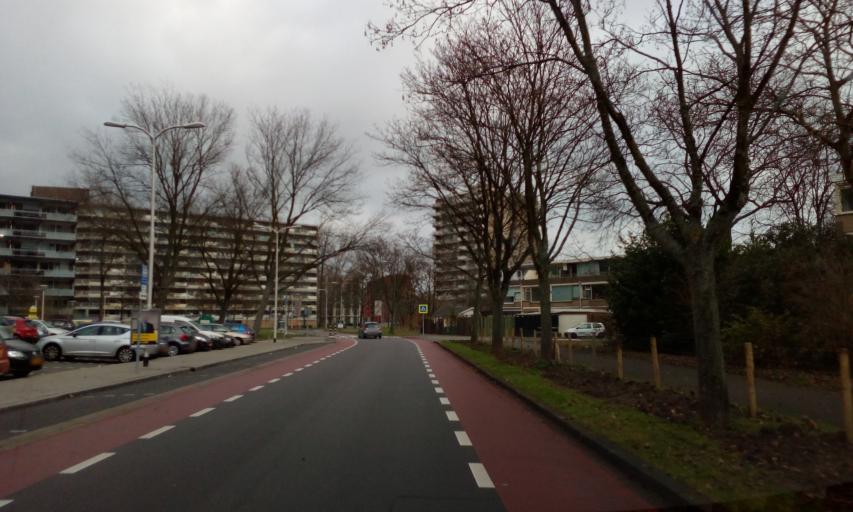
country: NL
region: South Holland
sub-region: Gemeente Zoetermeer
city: Zoetermeer
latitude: 52.0543
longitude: 4.4875
